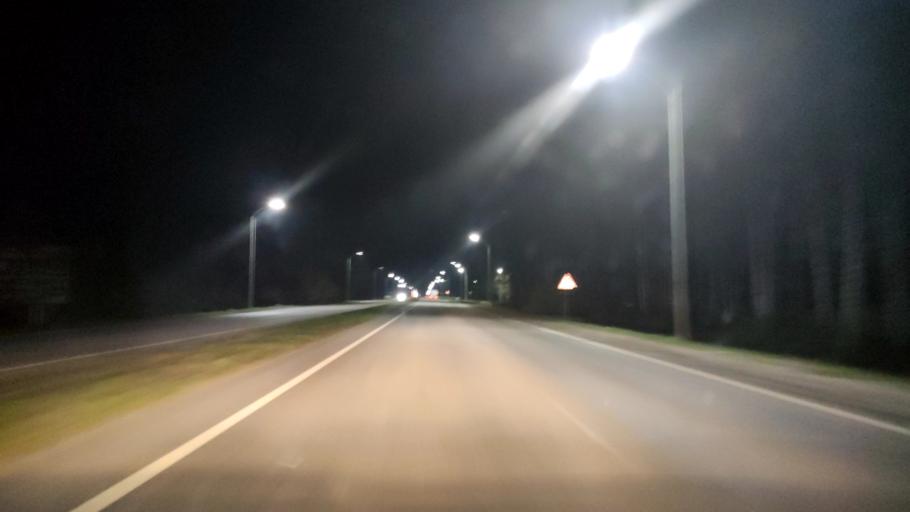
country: RU
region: Belgorod
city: Staryy Oskol
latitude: 51.3624
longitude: 37.8385
